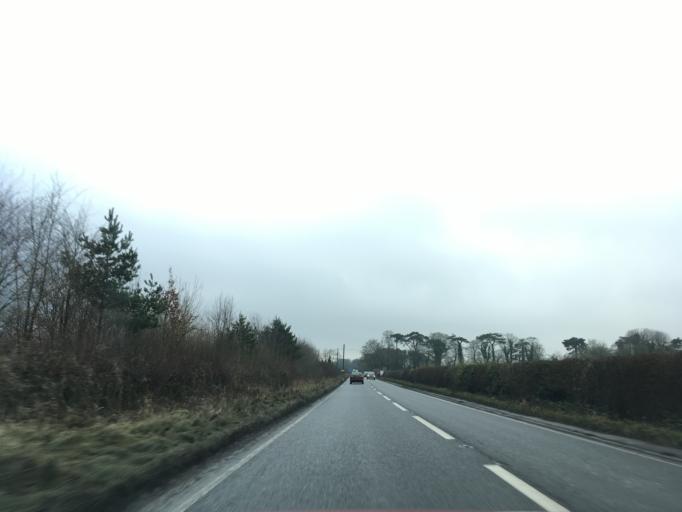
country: GB
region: England
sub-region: Gloucestershire
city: Cirencester
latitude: 51.7056
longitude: -1.9919
